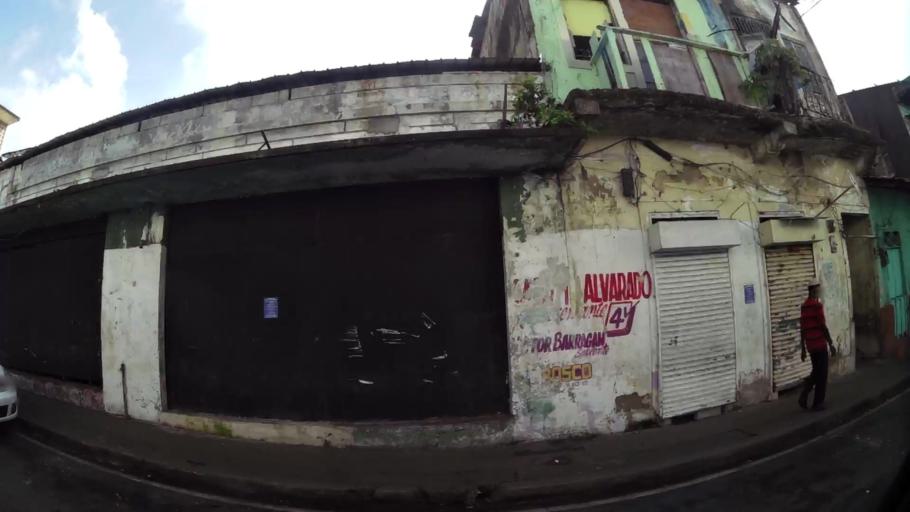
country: PA
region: Panama
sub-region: Distrito de Panama
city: Ancon
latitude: 8.9554
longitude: -79.5406
